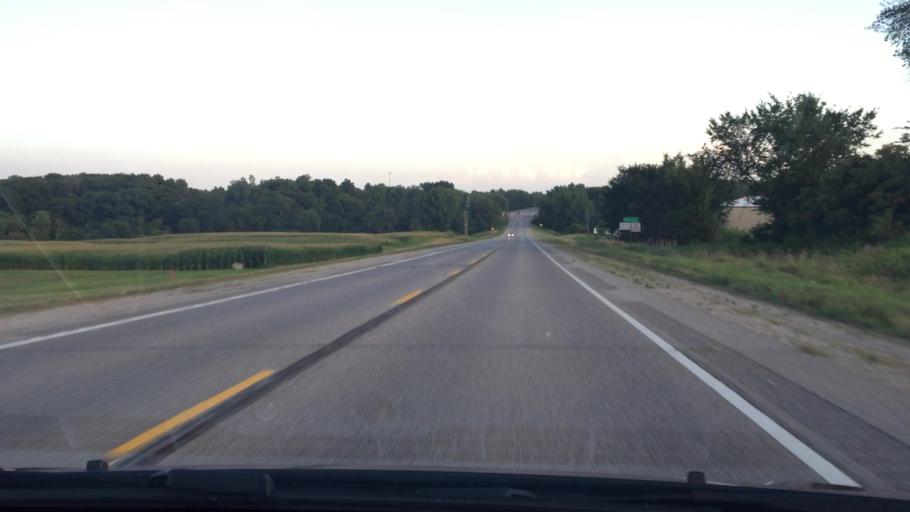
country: US
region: Iowa
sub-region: Muscatine County
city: Muscatine
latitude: 41.4650
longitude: -91.0340
